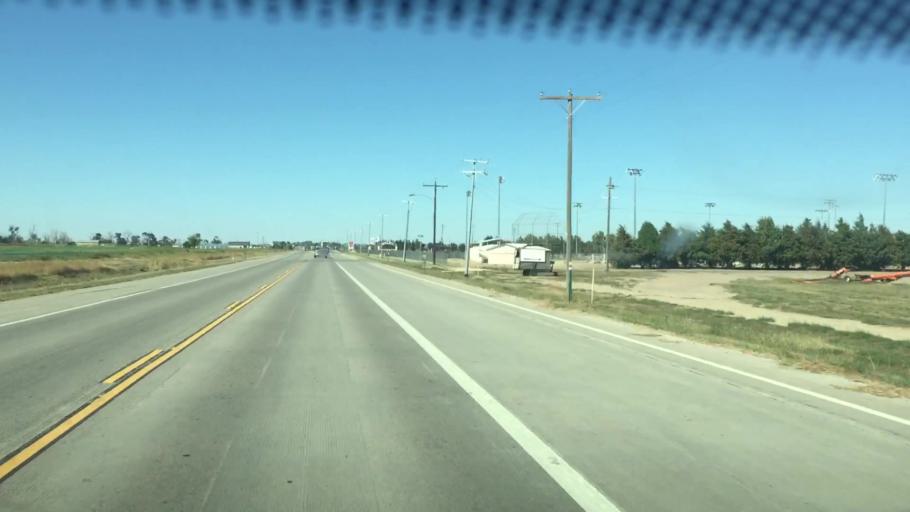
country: US
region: Colorado
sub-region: Prowers County
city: Lamar
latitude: 38.1527
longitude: -102.7237
